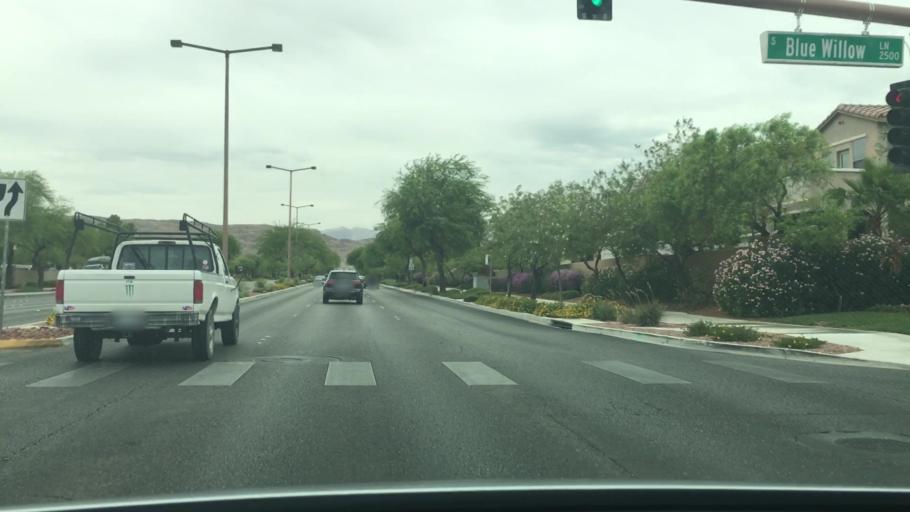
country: US
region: Nevada
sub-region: Clark County
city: Summerlin South
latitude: 36.1445
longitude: -115.3201
